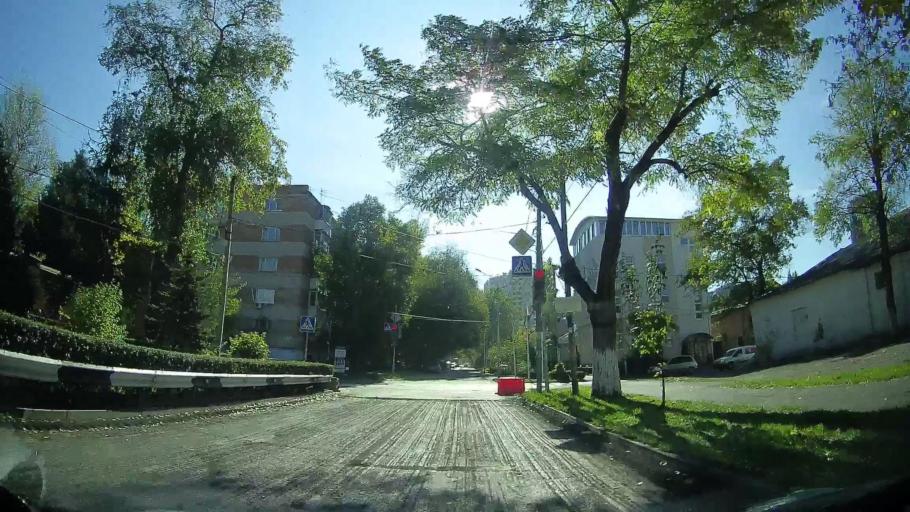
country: RU
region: Rostov
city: Rostov-na-Donu
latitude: 47.2362
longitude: 39.7298
